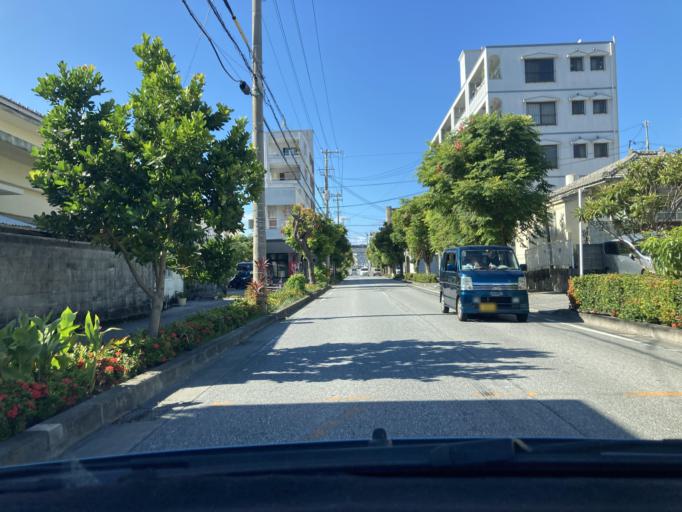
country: JP
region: Okinawa
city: Naha-shi
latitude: 26.2416
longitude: 127.6941
